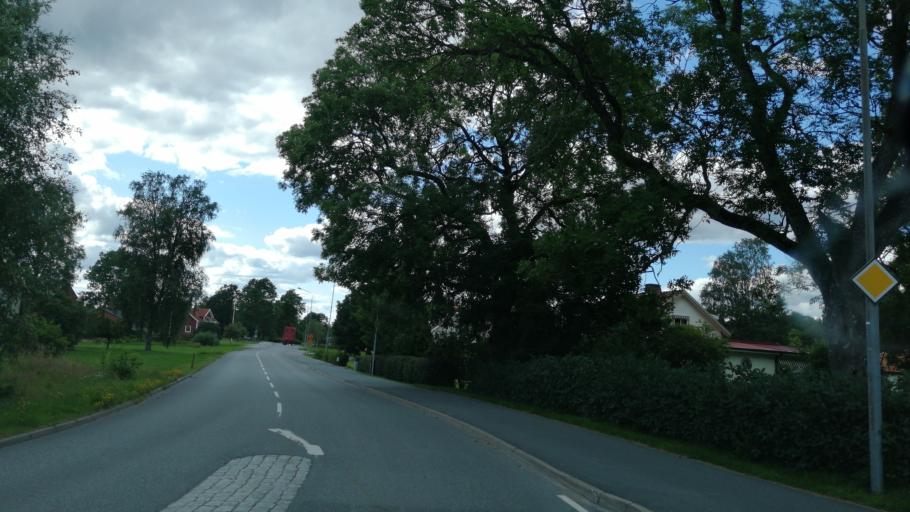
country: SE
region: Joenkoeping
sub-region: Gislaveds Kommun
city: Reftele
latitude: 57.1704
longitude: 13.6059
